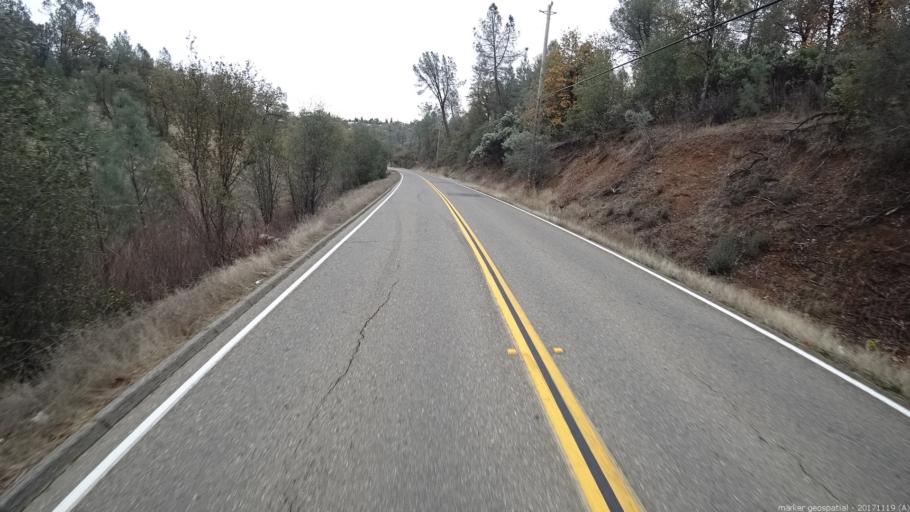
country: US
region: California
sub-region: Shasta County
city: Redding
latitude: 40.4891
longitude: -122.3962
